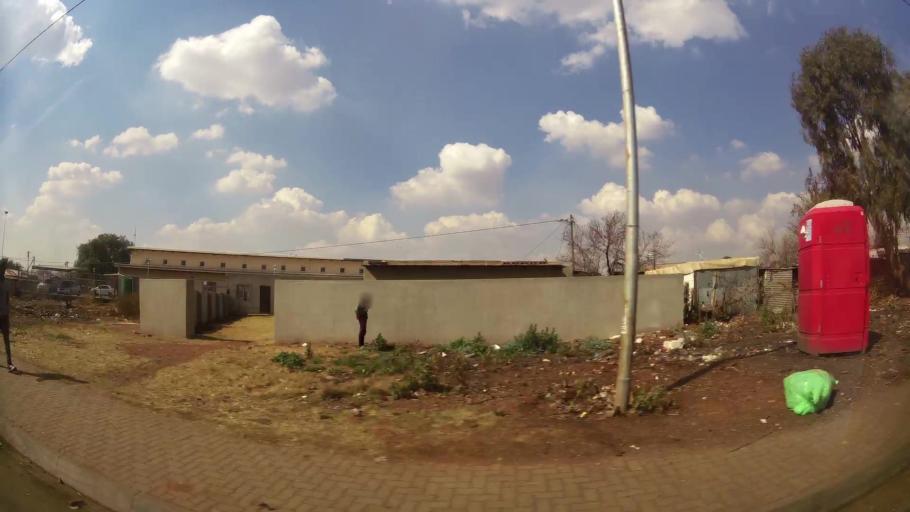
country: ZA
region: Gauteng
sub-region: Ekurhuleni Metropolitan Municipality
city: Germiston
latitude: -26.3096
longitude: 28.1477
